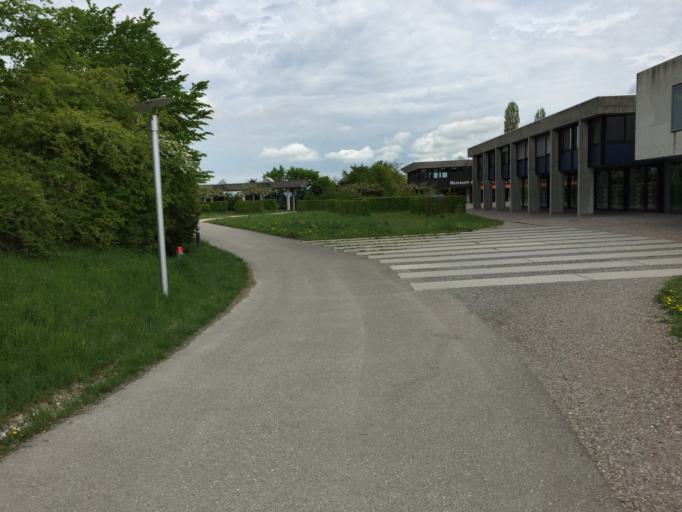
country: CH
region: Zurich
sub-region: Bezirk Zuerich
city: Zuerich (Kreis 6)
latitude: 47.3970
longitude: 8.5465
